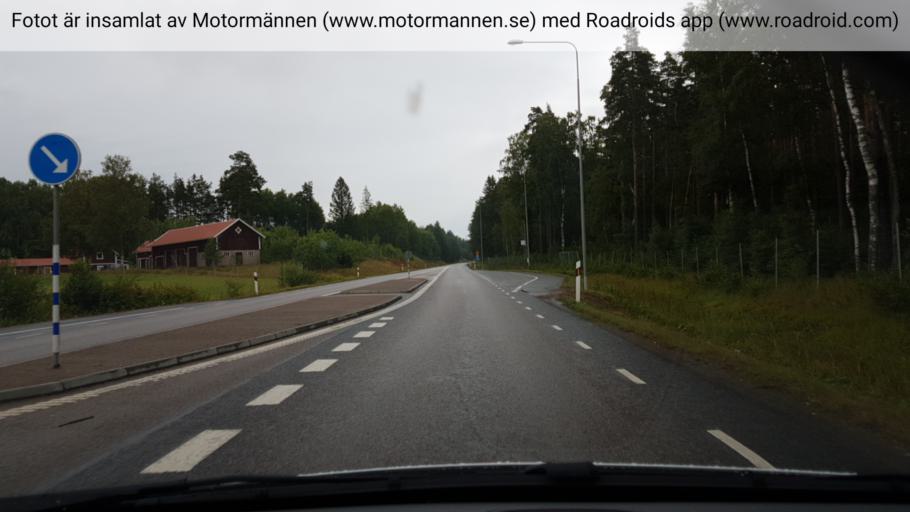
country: SE
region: Vaestra Goetaland
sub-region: Tibro Kommun
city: Tibro
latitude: 58.4447
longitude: 14.1867
